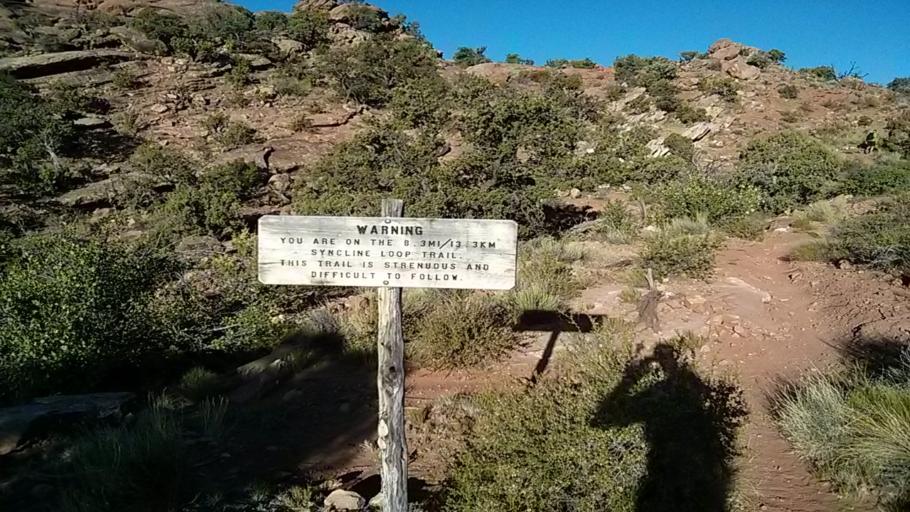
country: US
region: Utah
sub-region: Grand County
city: Moab
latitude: 38.4266
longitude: -109.9268
